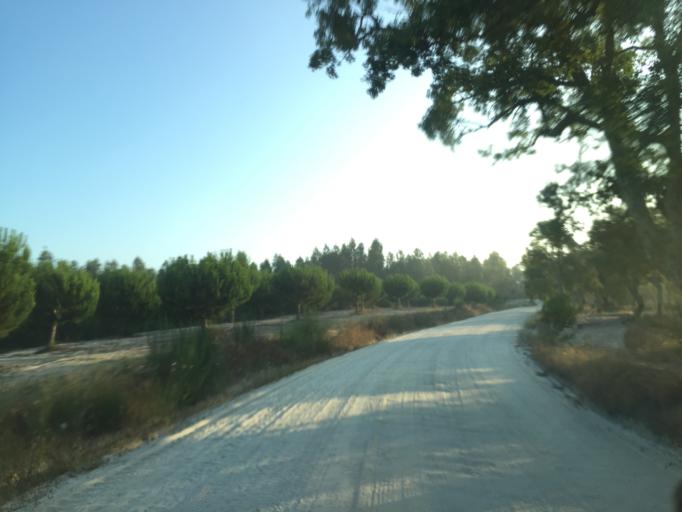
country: PT
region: Santarem
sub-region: Coruche
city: Coruche
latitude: 39.0627
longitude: -8.4076
